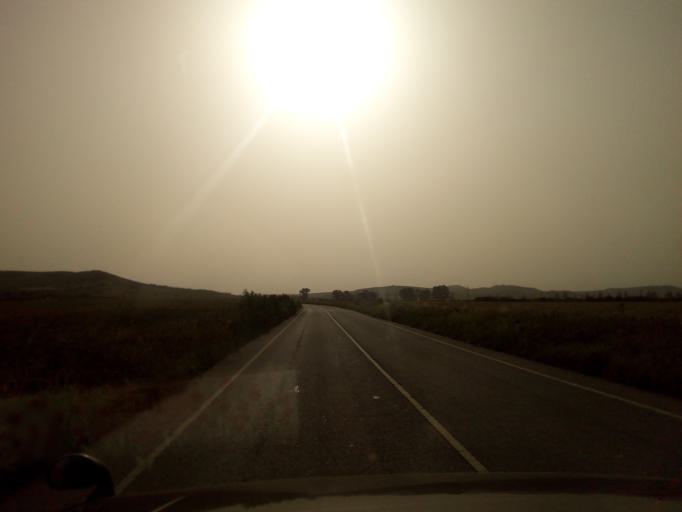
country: CY
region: Larnaka
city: Athienou
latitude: 35.0544
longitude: 33.5110
